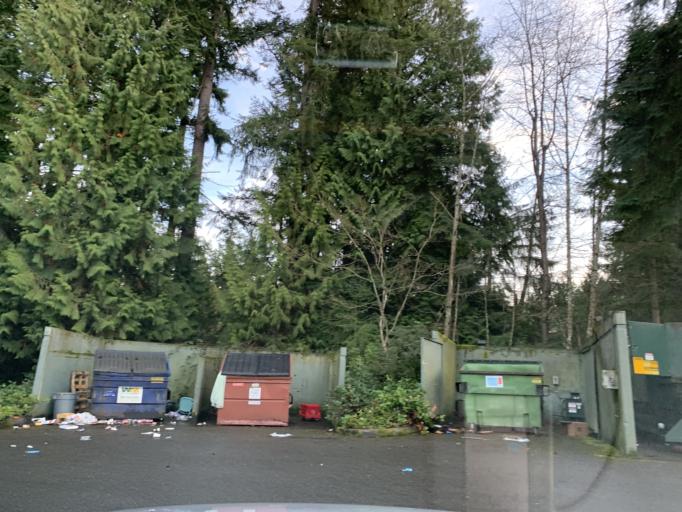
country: US
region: Washington
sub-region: King County
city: Redmond
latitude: 47.6398
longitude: -122.1242
